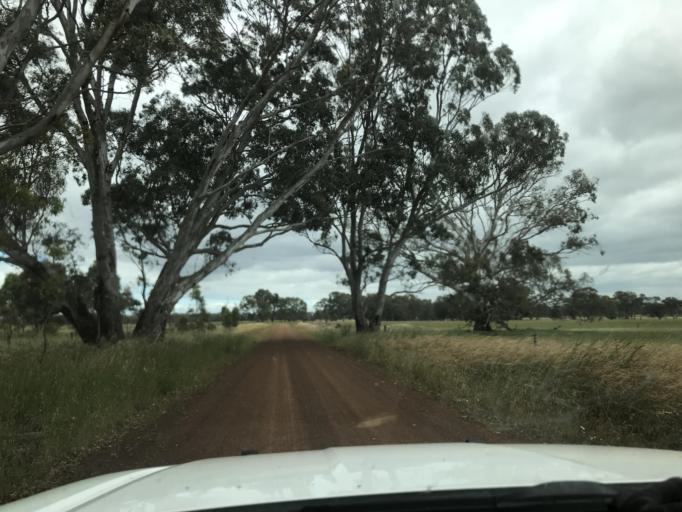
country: AU
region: South Australia
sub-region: Wattle Range
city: Penola
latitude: -37.1022
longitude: 141.2343
